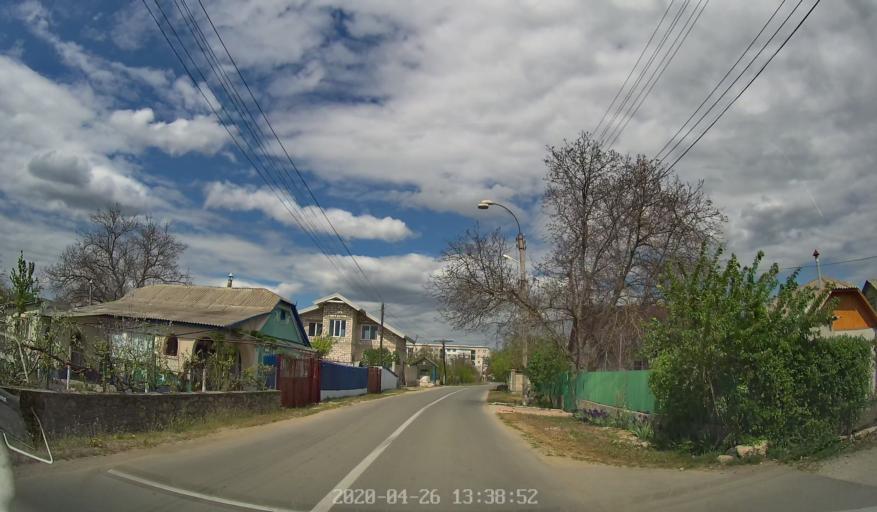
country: MD
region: Criuleni
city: Criuleni
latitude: 47.2109
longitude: 29.1650
